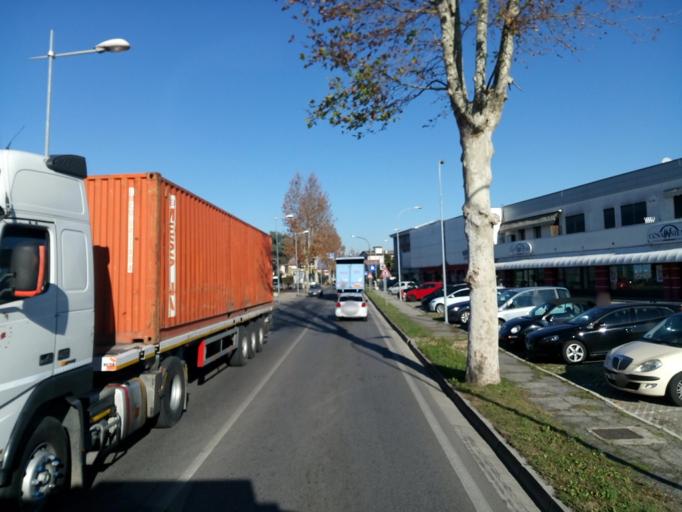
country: IT
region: Veneto
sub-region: Provincia di Treviso
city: Valla
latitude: 45.7035
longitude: 11.9297
